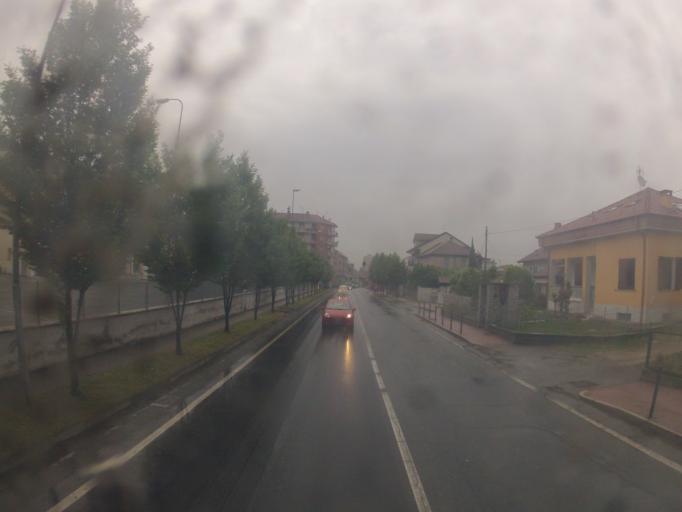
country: IT
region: Piedmont
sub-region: Provincia di Torino
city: La Loggia
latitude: 44.9526
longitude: 7.6686
